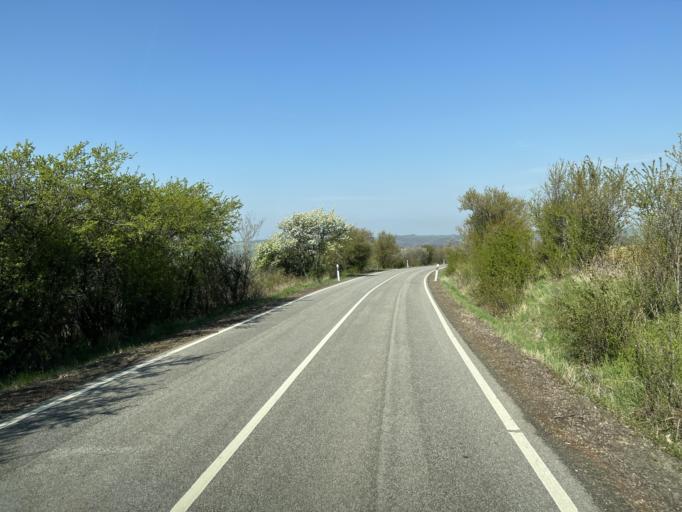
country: HU
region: Pest
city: Szob
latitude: 47.9372
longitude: 18.7928
